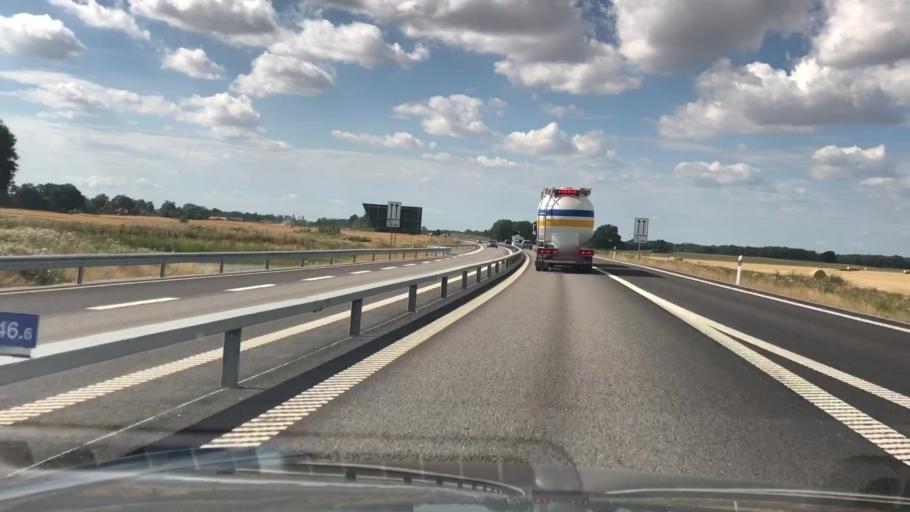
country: SE
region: Kalmar
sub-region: Kalmar Kommun
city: Rinkabyholm
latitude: 56.6620
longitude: 16.2575
